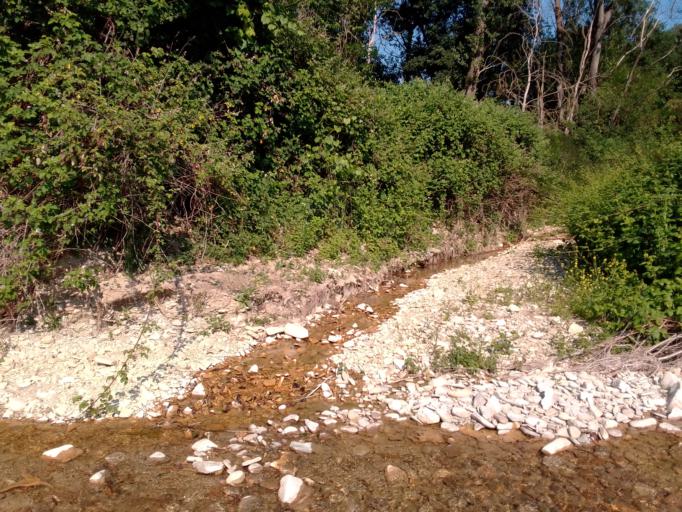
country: IT
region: Emilia-Romagna
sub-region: Provincia di Piacenza
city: Borgonovo Valtidone
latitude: 44.9778
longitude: 9.4602
